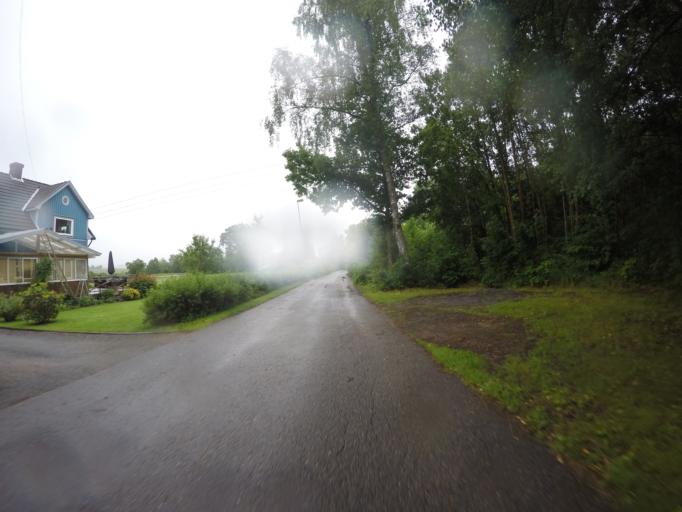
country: SE
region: Vaestra Goetaland
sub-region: Trollhattan
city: Sjuntorp
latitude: 58.1849
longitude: 12.2287
